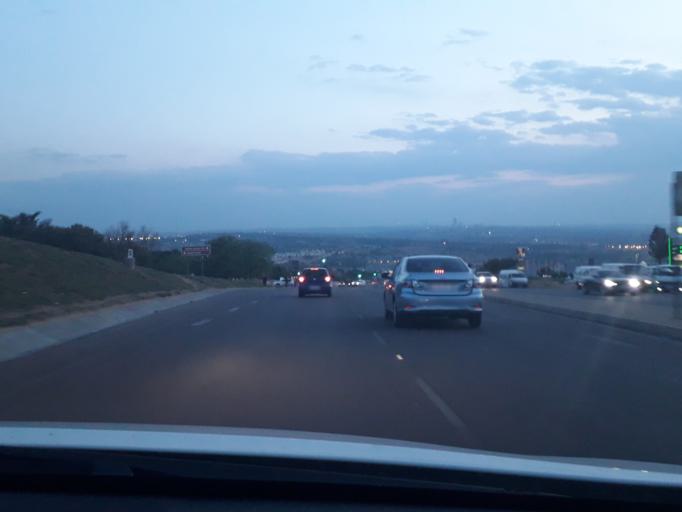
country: ZA
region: Gauteng
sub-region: City of Johannesburg Metropolitan Municipality
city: Midrand
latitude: -25.9879
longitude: 28.0768
